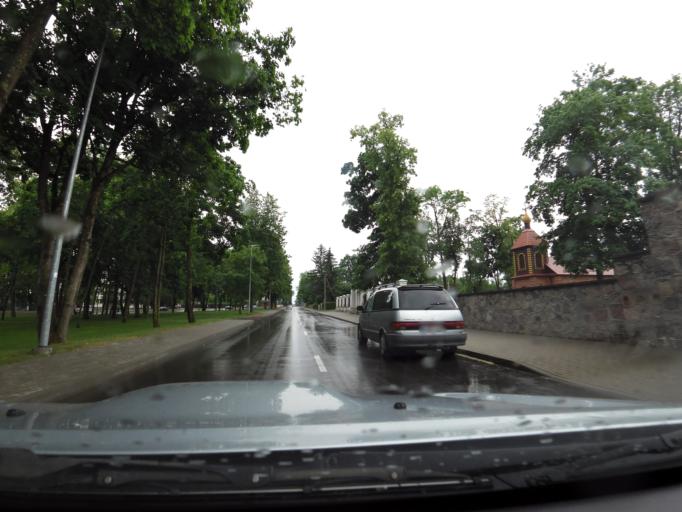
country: LT
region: Marijampoles apskritis
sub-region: Marijampole Municipality
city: Marijampole
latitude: 54.5489
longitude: 23.3465
